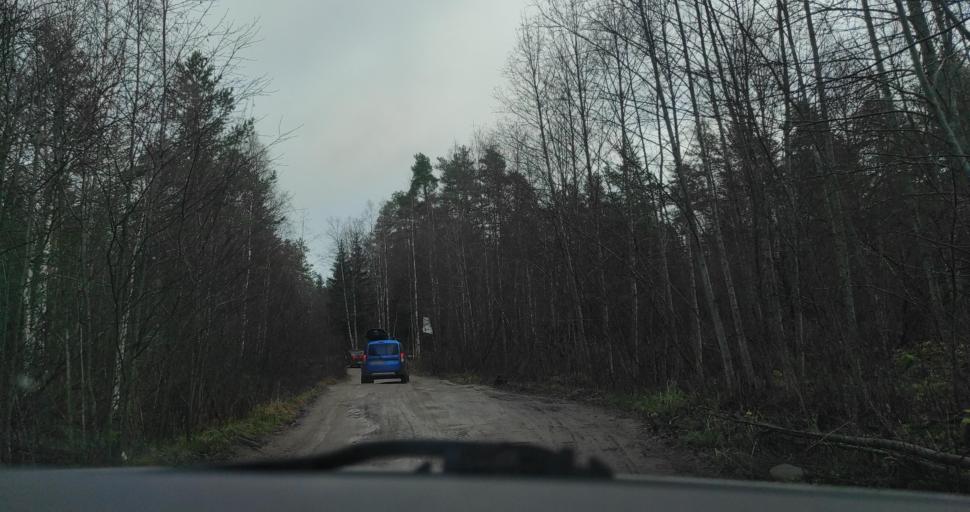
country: RU
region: Republic of Karelia
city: Pitkyaranta
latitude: 61.7365
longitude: 31.3872
